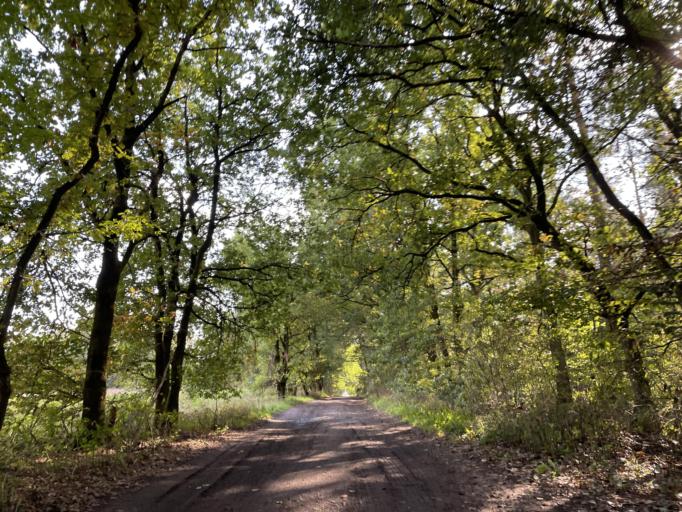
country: DE
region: Lower Saxony
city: Deutsch Evern
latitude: 53.2088
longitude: 10.4378
